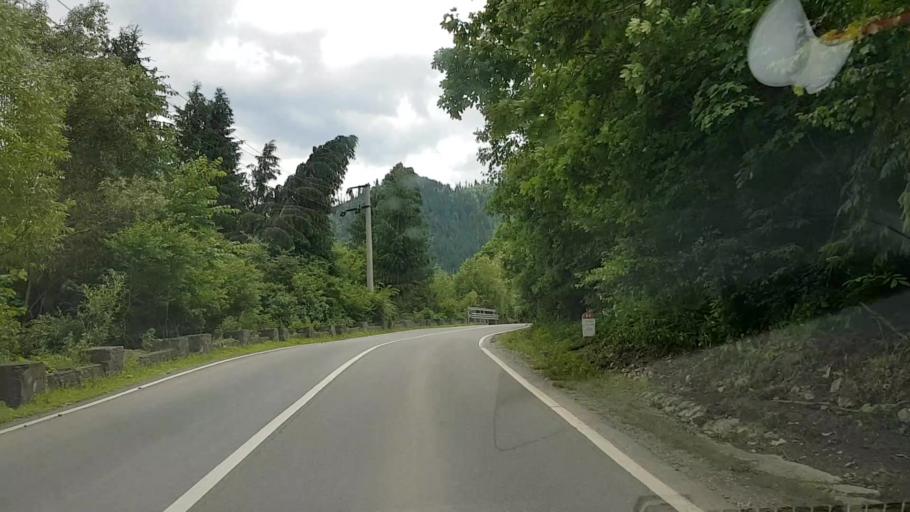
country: RO
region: Neamt
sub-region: Comuna Poiana Teiului
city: Poiana Teiului
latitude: 47.1010
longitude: 25.9411
